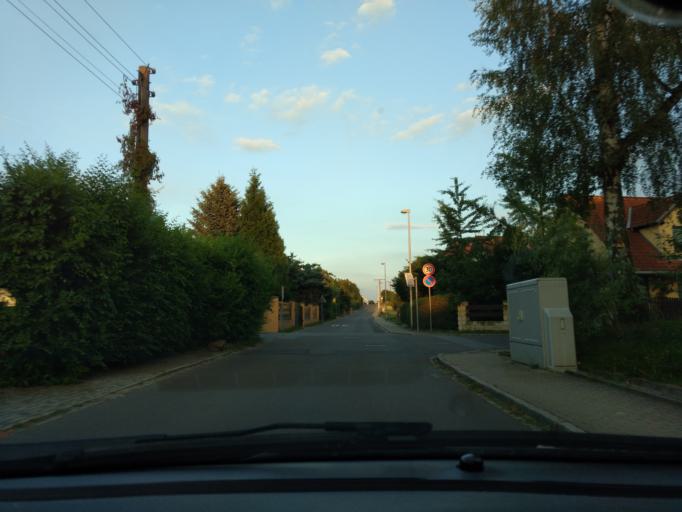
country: DE
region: Saxony
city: Radebeul
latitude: 51.1188
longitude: 13.6717
